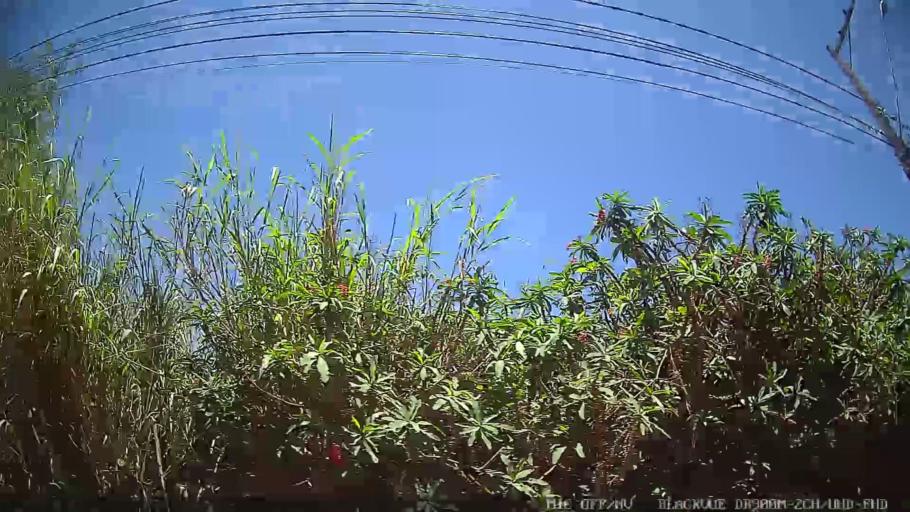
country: BR
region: Sao Paulo
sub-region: Jaguariuna
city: Jaguariuna
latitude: -22.7448
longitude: -47.0040
